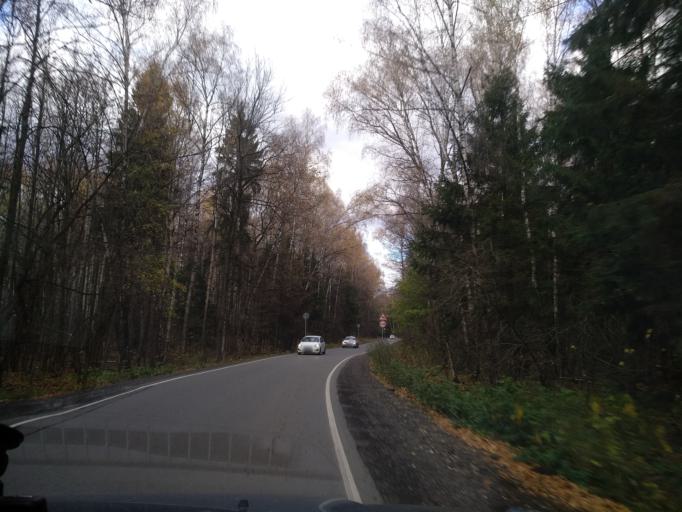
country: RU
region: Moscow
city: Lianozovo
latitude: 55.9099
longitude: 37.6106
